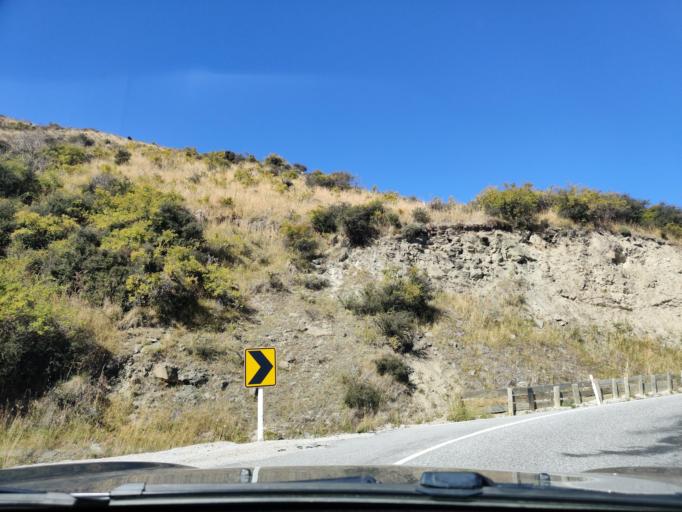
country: NZ
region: Otago
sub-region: Queenstown-Lakes District
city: Arrowtown
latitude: -44.9916
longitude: 168.9091
